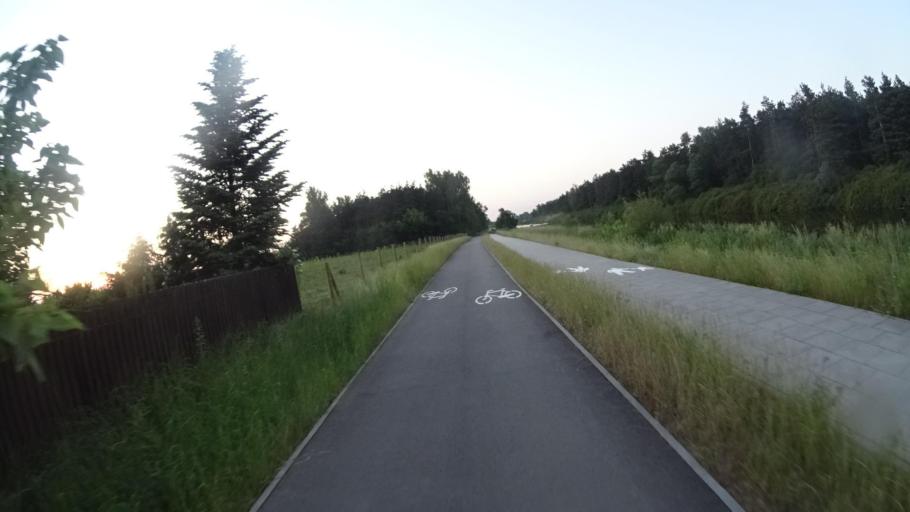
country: PL
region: Masovian Voivodeship
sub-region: Powiat legionowski
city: Stanislawow Pierwszy
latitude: 52.3660
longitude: 21.0325
